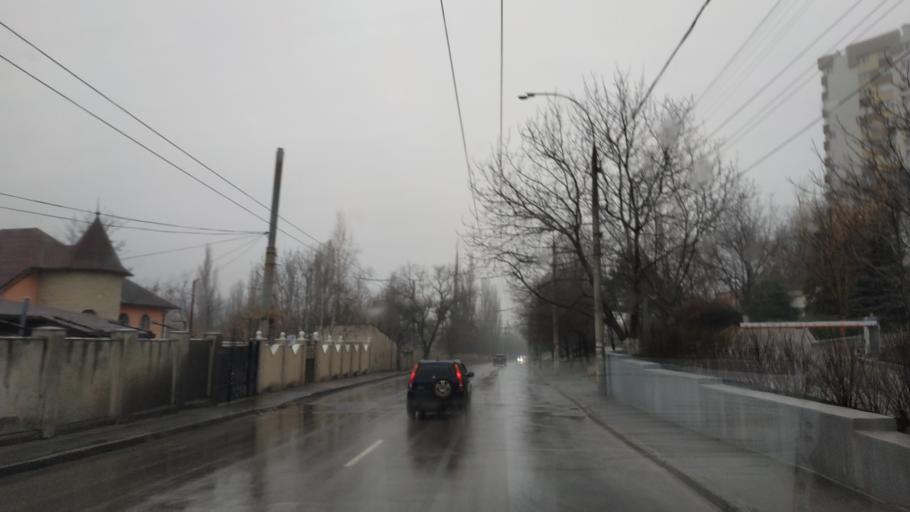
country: MD
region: Chisinau
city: Chisinau
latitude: 47.0236
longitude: 28.7892
